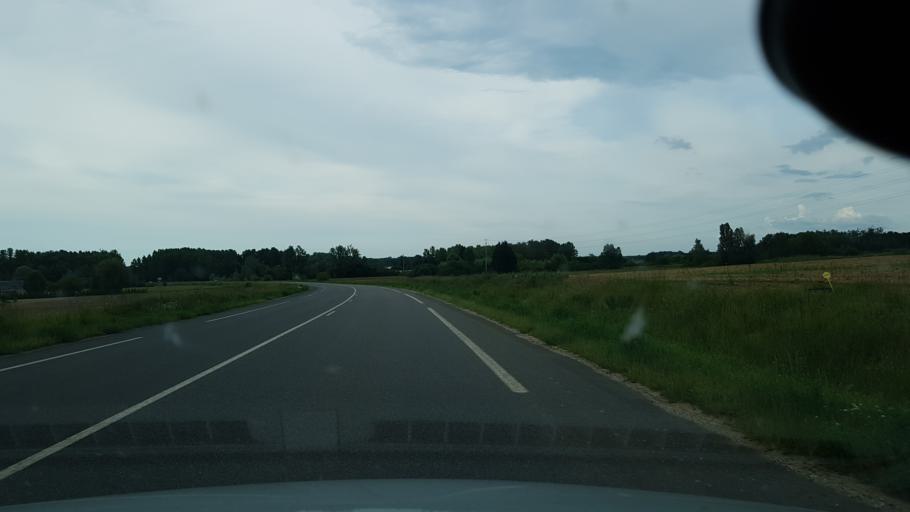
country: FR
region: Centre
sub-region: Departement du Loir-et-Cher
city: Contres
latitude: 47.4143
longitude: 1.4498
